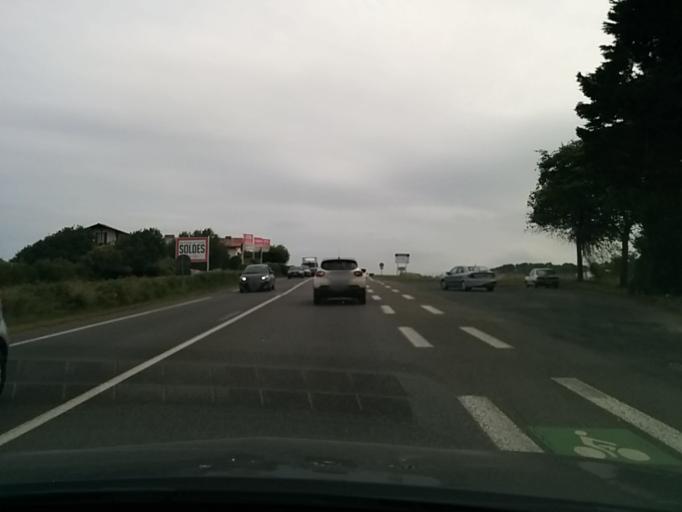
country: FR
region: Aquitaine
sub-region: Departement des Pyrenees-Atlantiques
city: Guethary
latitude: 43.4061
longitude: -1.6289
